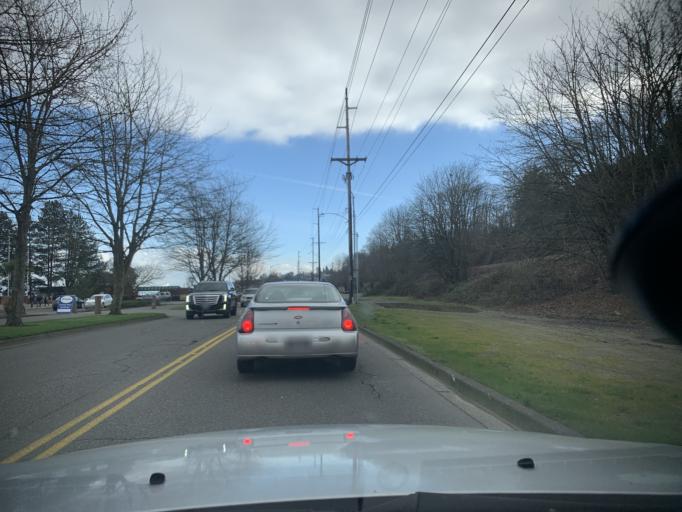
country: US
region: Washington
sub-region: Pierce County
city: Tacoma
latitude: 47.2820
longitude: -122.4806
